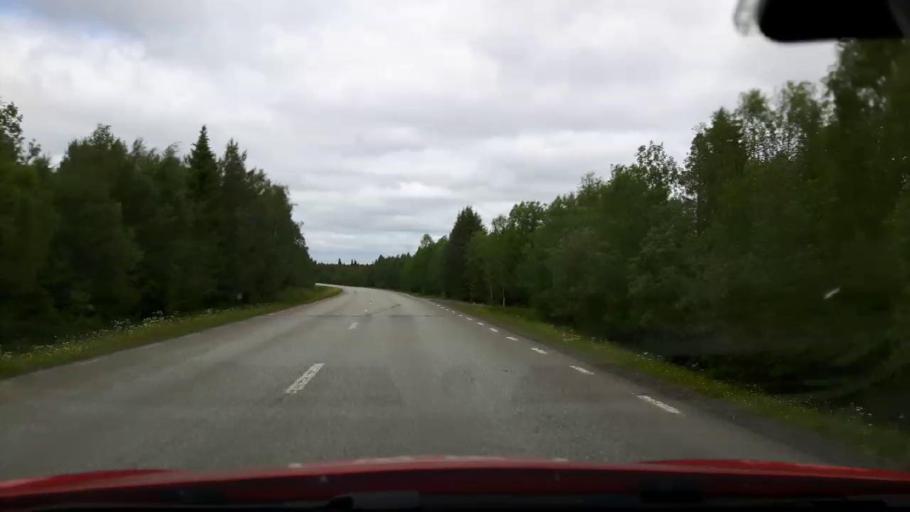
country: SE
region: Jaemtland
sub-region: Krokoms Kommun
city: Krokom
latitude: 63.3816
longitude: 14.5073
